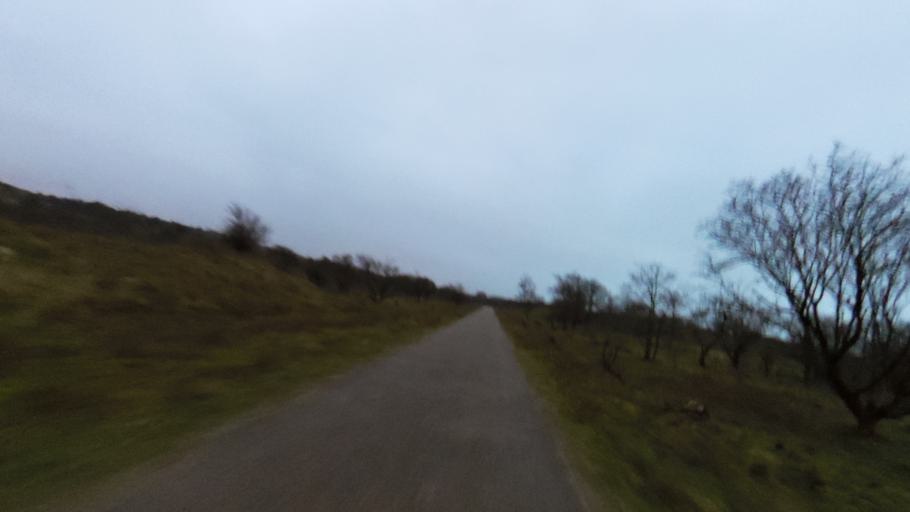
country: NL
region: North Holland
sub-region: Gemeente Beverwijk
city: Beverwijk
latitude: 52.5044
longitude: 4.6057
